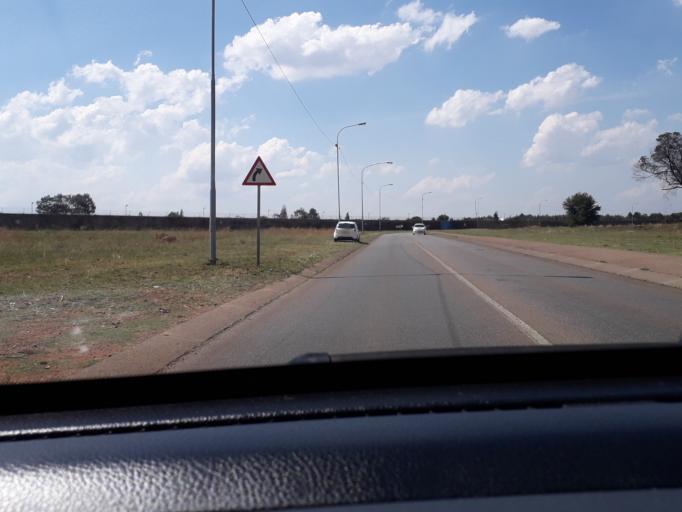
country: ZA
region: Gauteng
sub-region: City of Tshwane Metropolitan Municipality
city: Centurion
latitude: -25.8474
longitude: 28.2267
